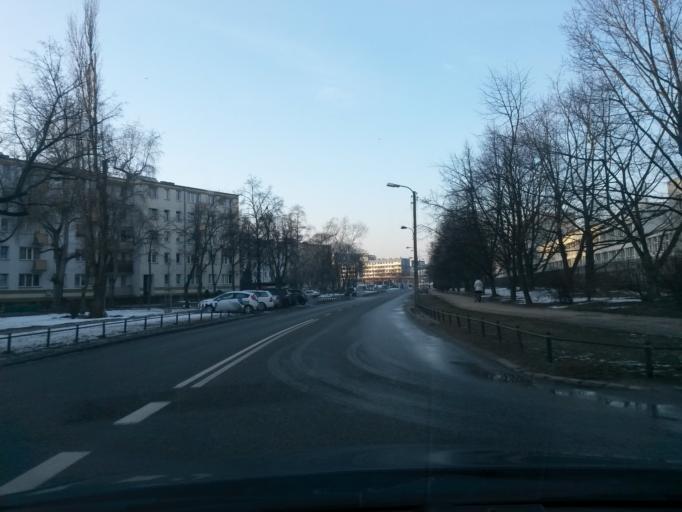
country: PL
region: Masovian Voivodeship
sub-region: Warszawa
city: Mokotow
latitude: 52.1754
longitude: 21.0091
